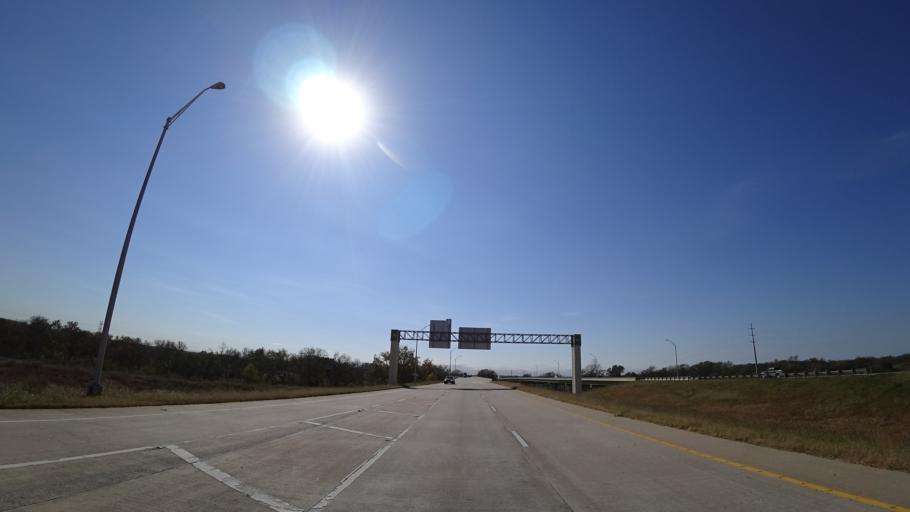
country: US
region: Texas
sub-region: Travis County
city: Garfield
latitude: 30.1906
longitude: -97.6257
